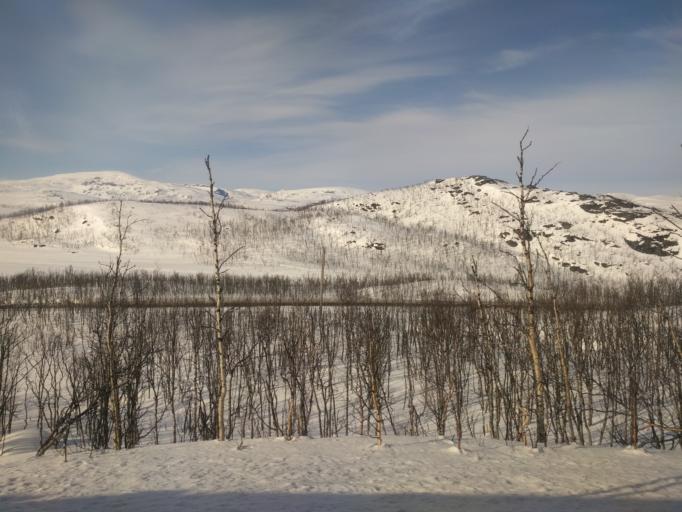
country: NO
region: Troms
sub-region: Bardu
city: Setermoen
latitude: 68.4255
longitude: 18.4307
